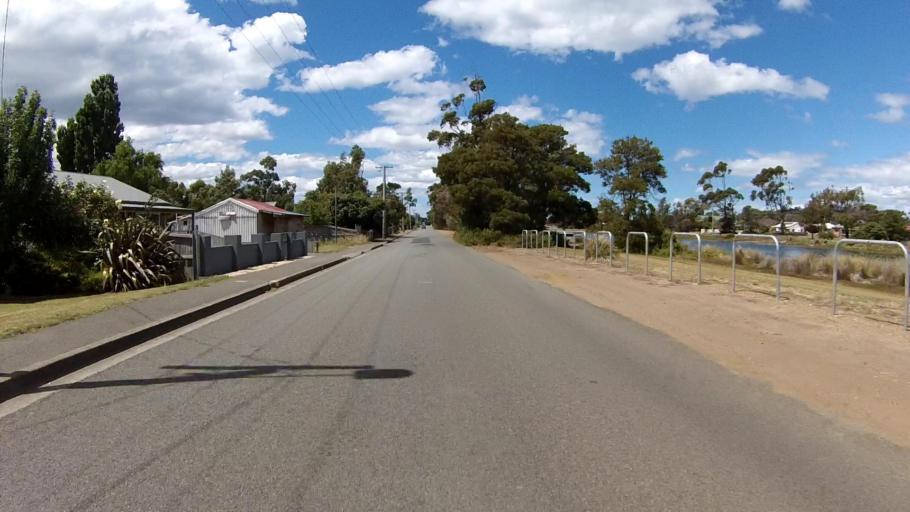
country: AU
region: Tasmania
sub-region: Clarence
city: Lauderdale
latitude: -42.9121
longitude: 147.4880
